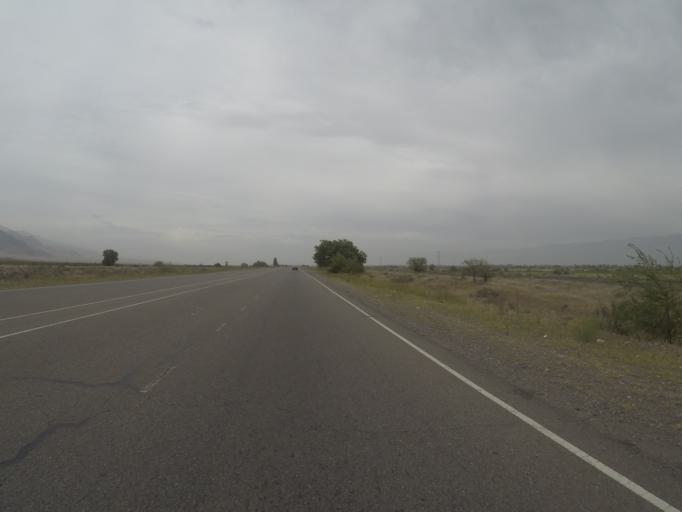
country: KG
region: Chuy
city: Tokmok
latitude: 42.8313
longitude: 75.4548
